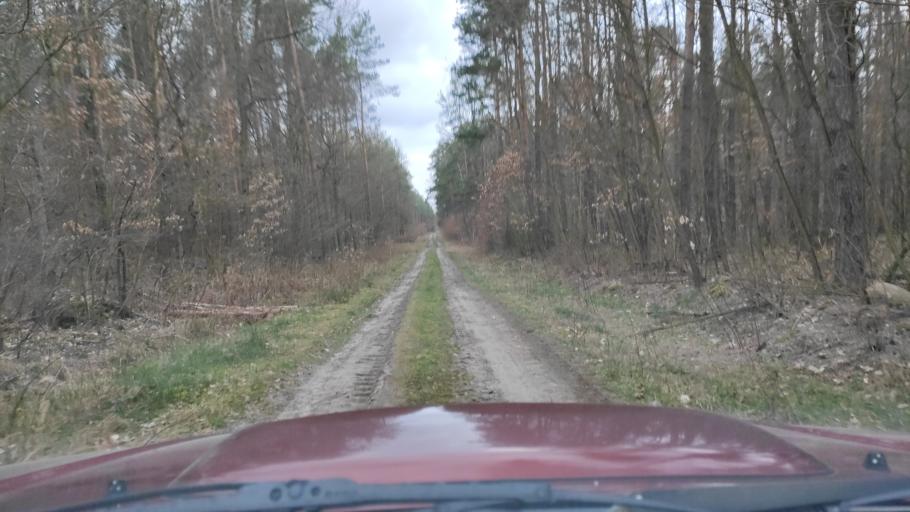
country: PL
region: Masovian Voivodeship
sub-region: Powiat kozienicki
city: Garbatka-Letnisko
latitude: 51.5069
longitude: 21.5540
